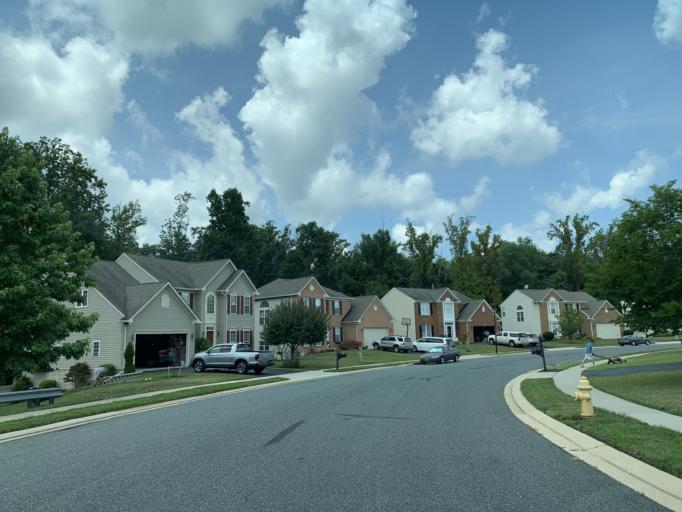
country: US
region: Maryland
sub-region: Harford County
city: Bel Air North
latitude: 39.5557
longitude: -76.3615
